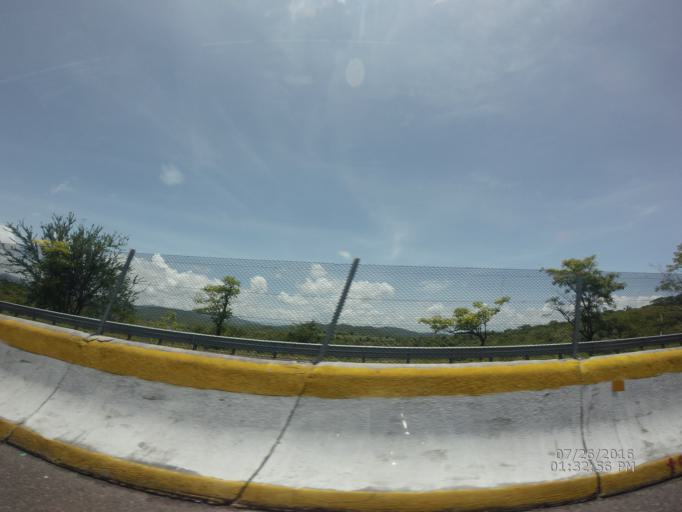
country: MX
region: Guerrero
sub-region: Huitzuco de los Figueroa
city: Ciudad de Huitzuco
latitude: 18.2063
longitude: -99.2097
